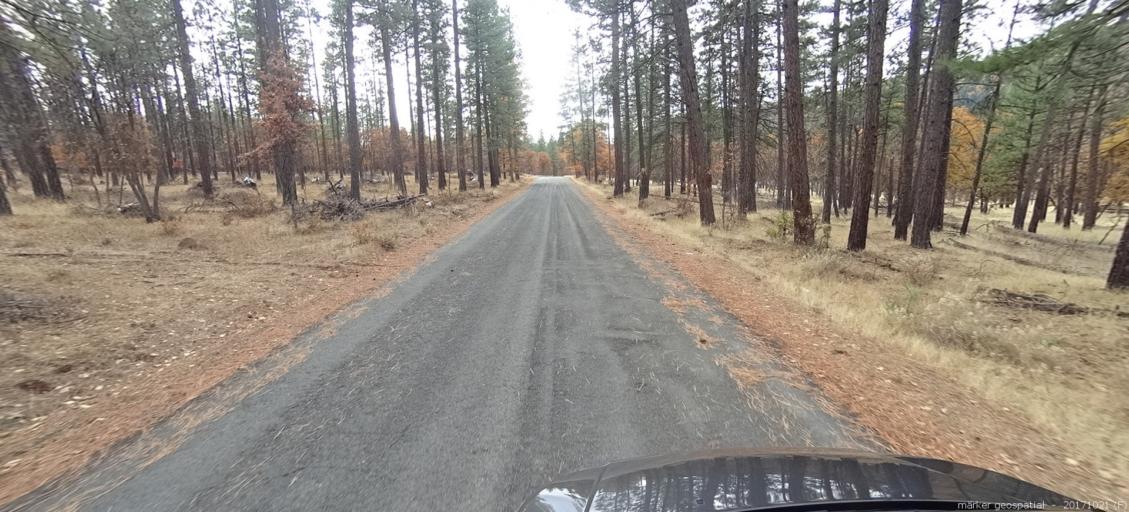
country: US
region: California
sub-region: Shasta County
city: Burney
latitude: 40.9507
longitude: -121.6436
